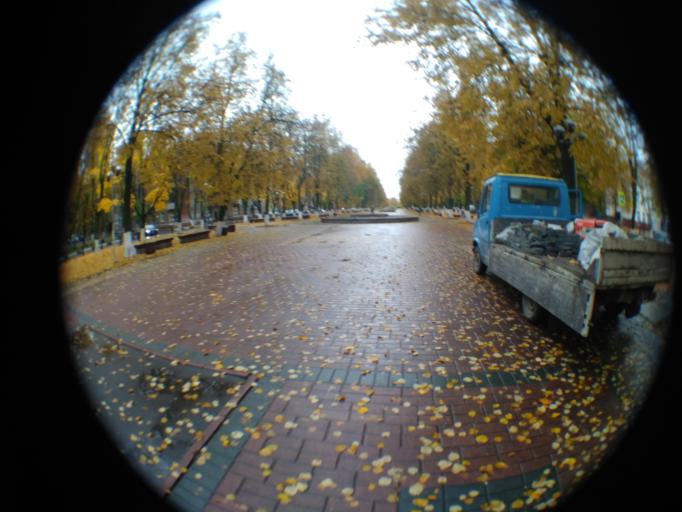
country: RU
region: Moskovskaya
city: Zhukovskiy
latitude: 55.5957
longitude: 38.1213
